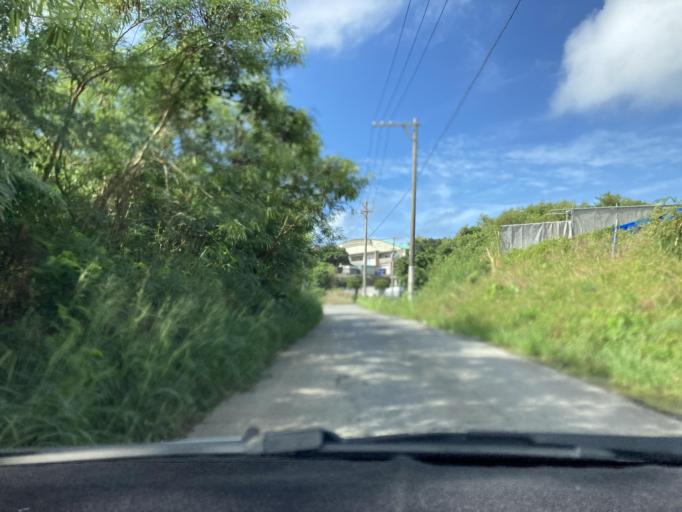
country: JP
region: Okinawa
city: Itoman
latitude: 26.0954
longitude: 127.6663
